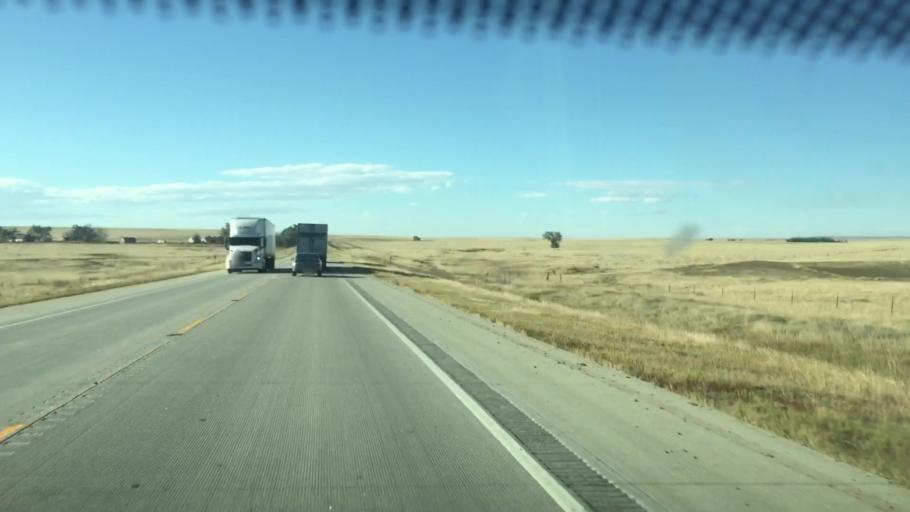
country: US
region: Colorado
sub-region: Lincoln County
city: Hugo
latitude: 38.9322
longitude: -103.1997
